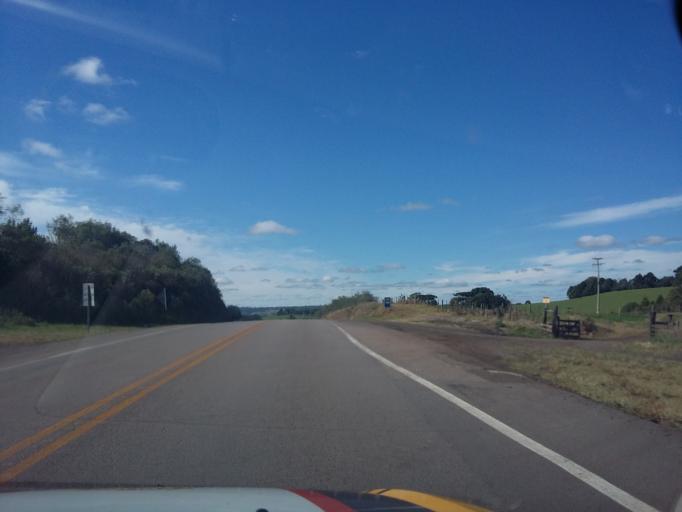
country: BR
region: Rio Grande do Sul
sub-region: Vacaria
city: Vacaria
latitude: -28.6525
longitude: -51.0505
